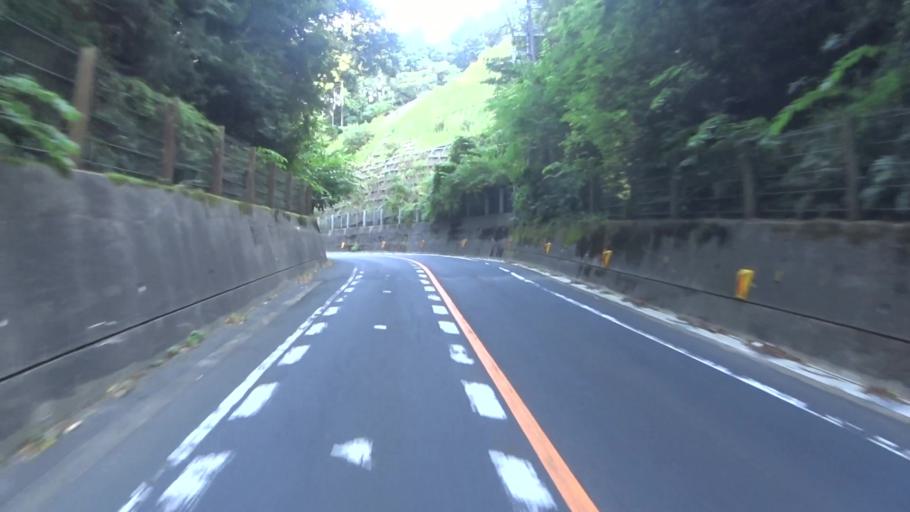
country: JP
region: Hyogo
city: Toyooka
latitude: 35.5936
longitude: 134.9135
